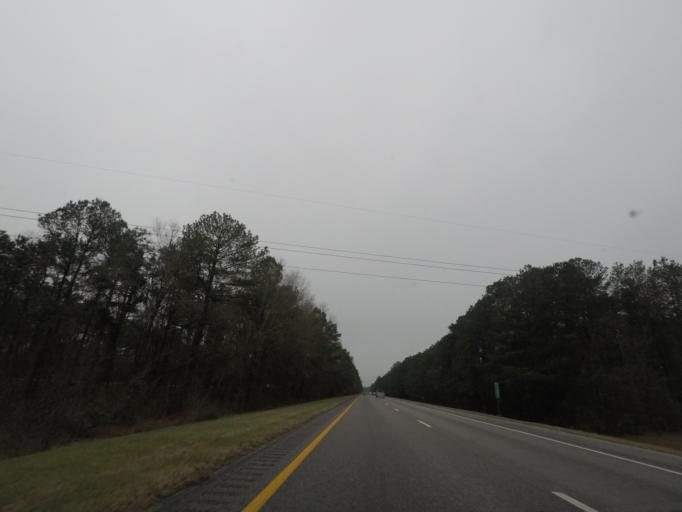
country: US
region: South Carolina
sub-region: Sumter County
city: East Sumter
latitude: 33.9229
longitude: -80.0770
